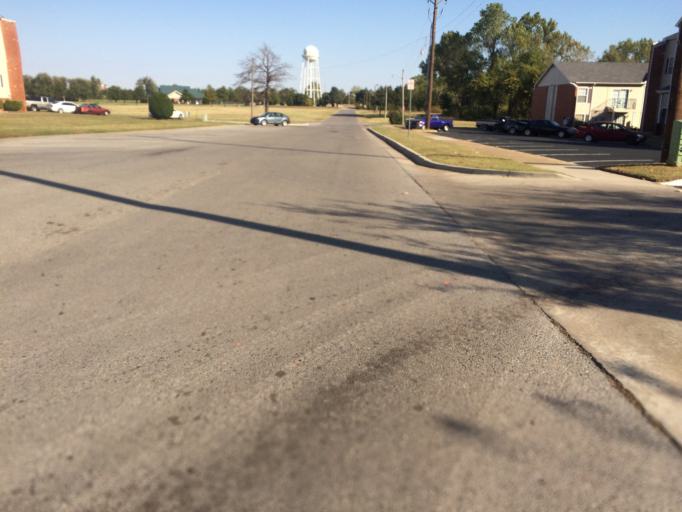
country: US
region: Oklahoma
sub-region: Cleveland County
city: Norman
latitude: 35.1883
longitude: -97.4322
